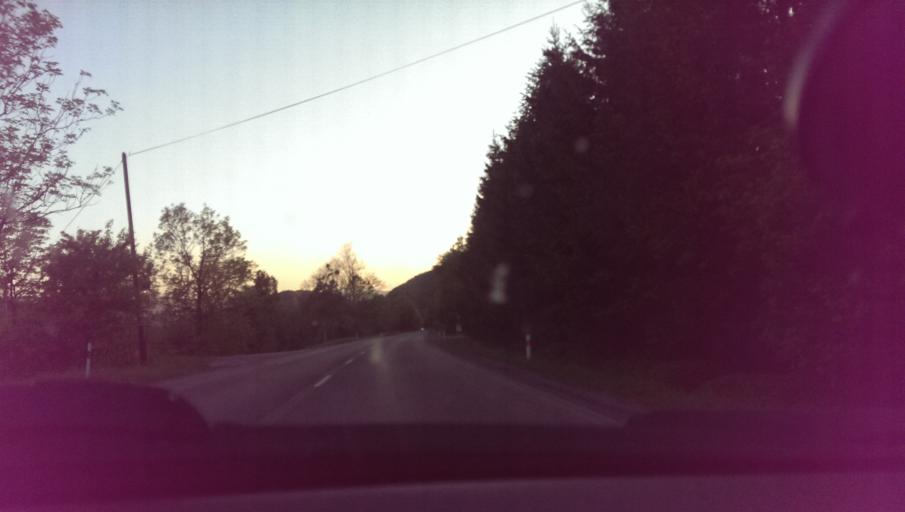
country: CZ
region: Zlin
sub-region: Okres Vsetin
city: Dolni Becva
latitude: 49.4974
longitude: 18.1828
